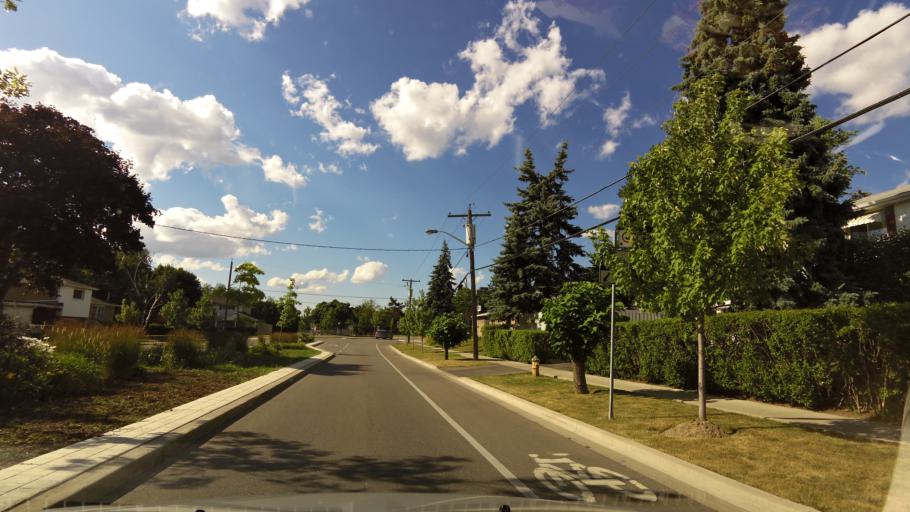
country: CA
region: Ontario
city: Willowdale
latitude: 43.7744
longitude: -79.3536
